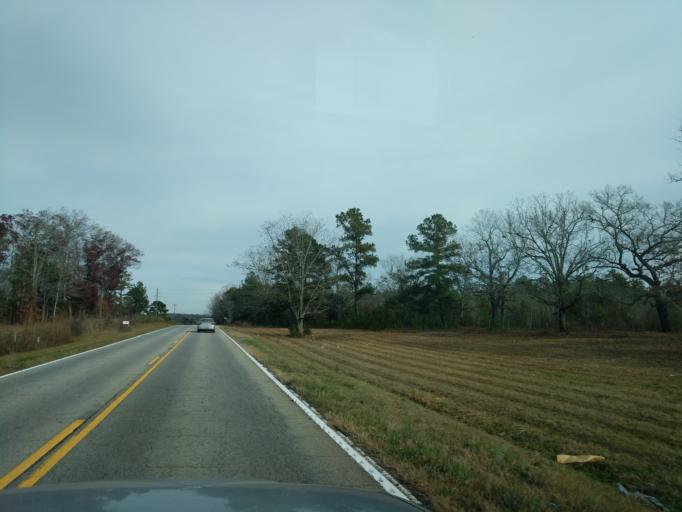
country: US
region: South Carolina
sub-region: Pickens County
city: Central
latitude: 34.7005
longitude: -82.7333
